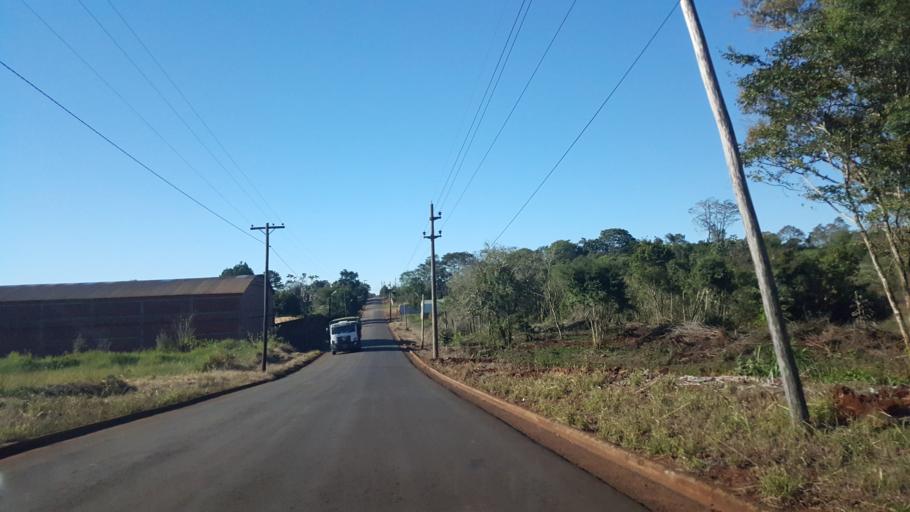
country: AR
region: Misiones
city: Gobernador Roca
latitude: -27.1846
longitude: -55.4612
